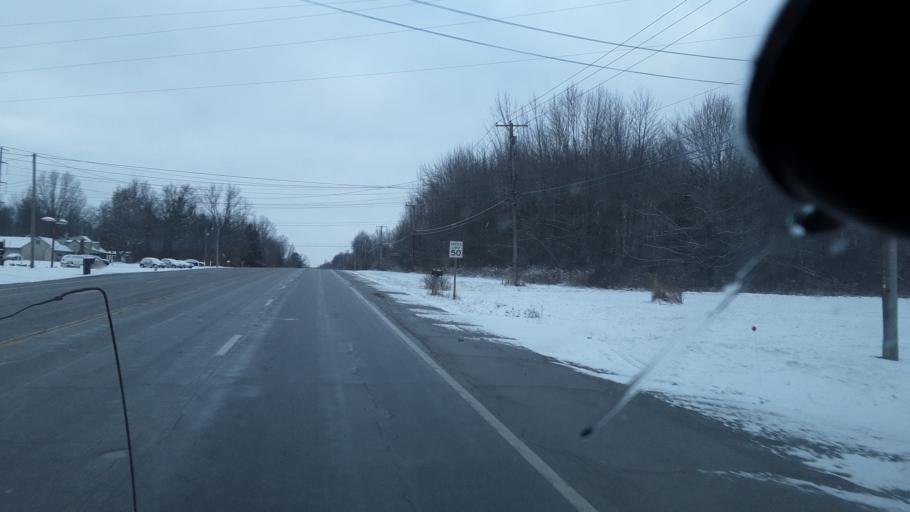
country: US
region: Ohio
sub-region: Trumbull County
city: Lordstown
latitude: 41.1407
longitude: -80.8572
